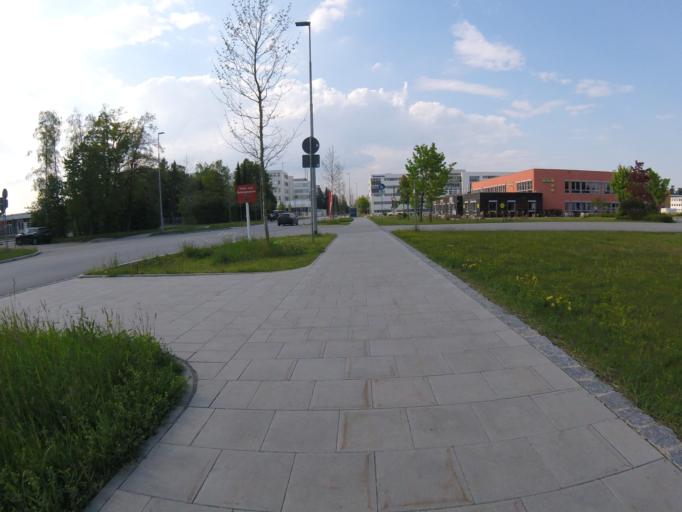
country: DE
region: Bavaria
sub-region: Upper Bavaria
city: Ottobrunn
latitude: 48.0507
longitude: 11.6554
